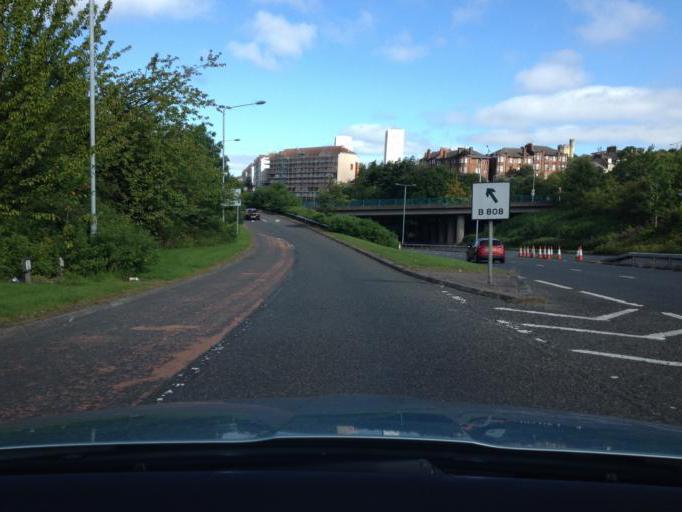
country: GB
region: Scotland
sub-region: East Dunbartonshire
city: Bishopbriggs
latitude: 55.8840
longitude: -4.2322
